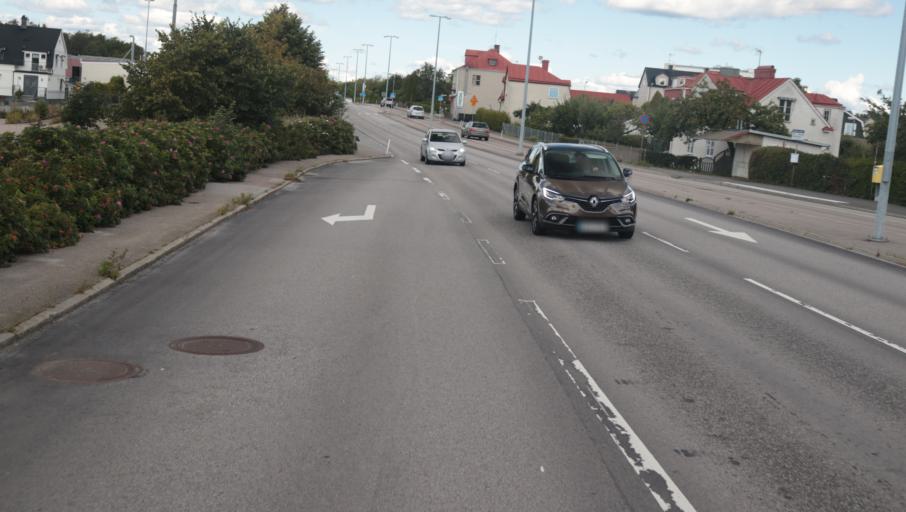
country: SE
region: Blekinge
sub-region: Karlshamns Kommun
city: Karlshamn
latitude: 56.1809
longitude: 14.8526
